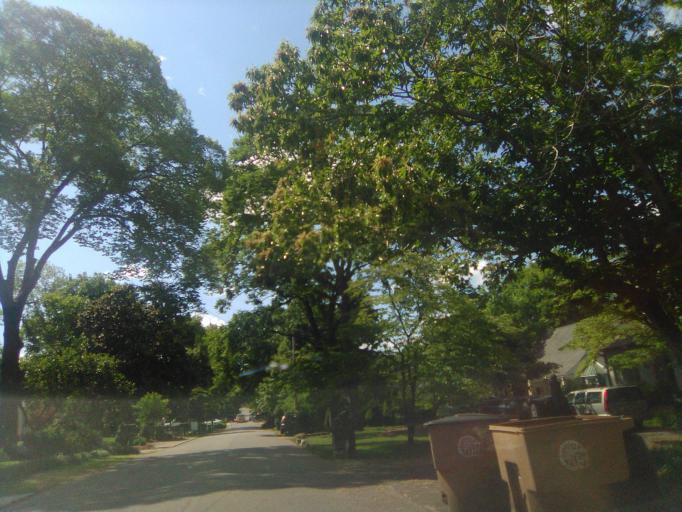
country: US
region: Tennessee
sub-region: Davidson County
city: Belle Meade
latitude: 36.1007
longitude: -86.8650
